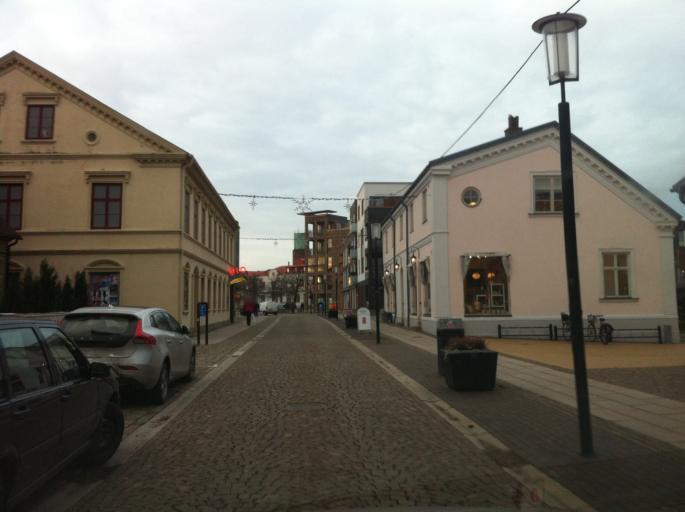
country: SE
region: Skane
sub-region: Hoganas Kommun
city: Hoganas
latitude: 56.2009
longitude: 12.5525
